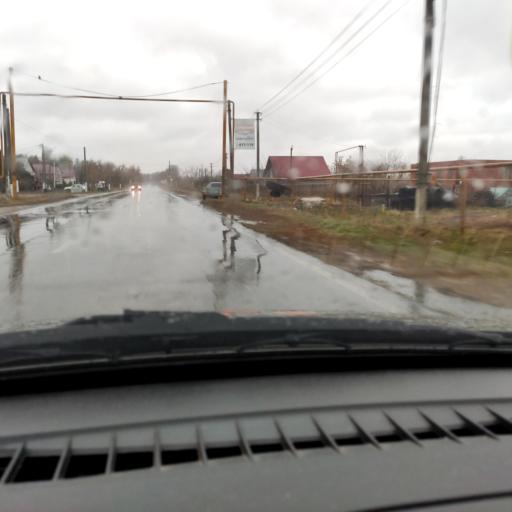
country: RU
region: Samara
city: Tol'yatti
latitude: 53.6495
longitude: 49.2923
